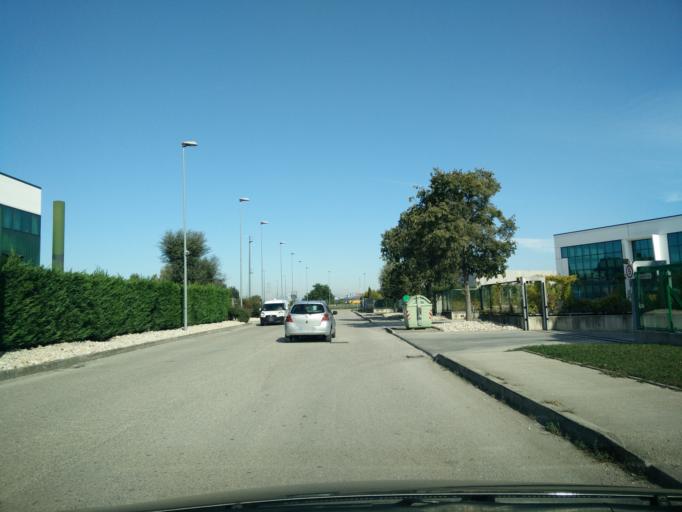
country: IT
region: Veneto
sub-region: Provincia di Venezia
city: Mestre
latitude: 45.4479
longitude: 12.2077
